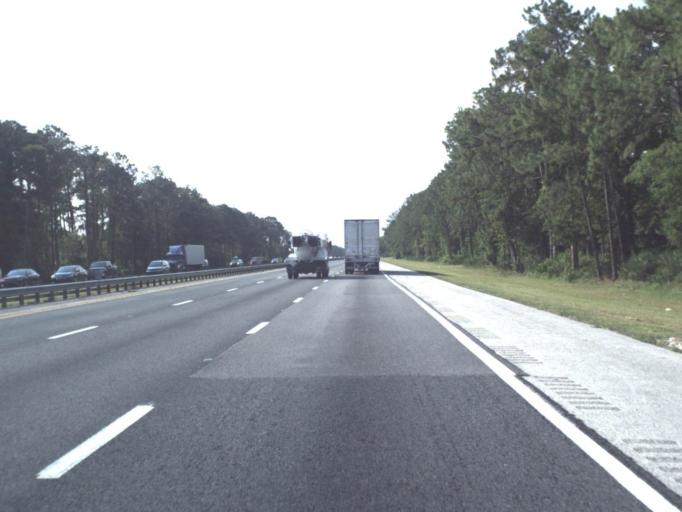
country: US
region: Florida
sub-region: Saint Johns County
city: Saint Augustine Shores
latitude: 29.7738
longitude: -81.3568
